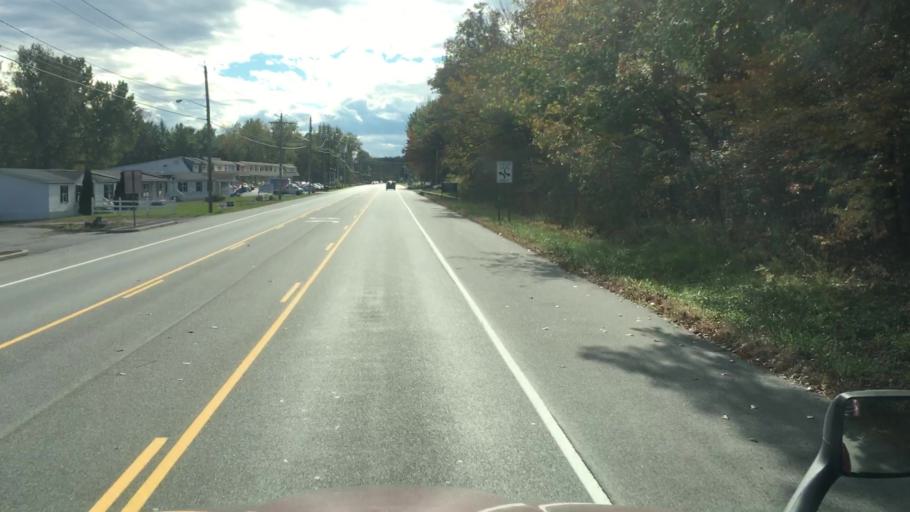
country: US
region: New York
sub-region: Saratoga County
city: North Ballston Spa
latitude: 43.0179
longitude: -73.8435
